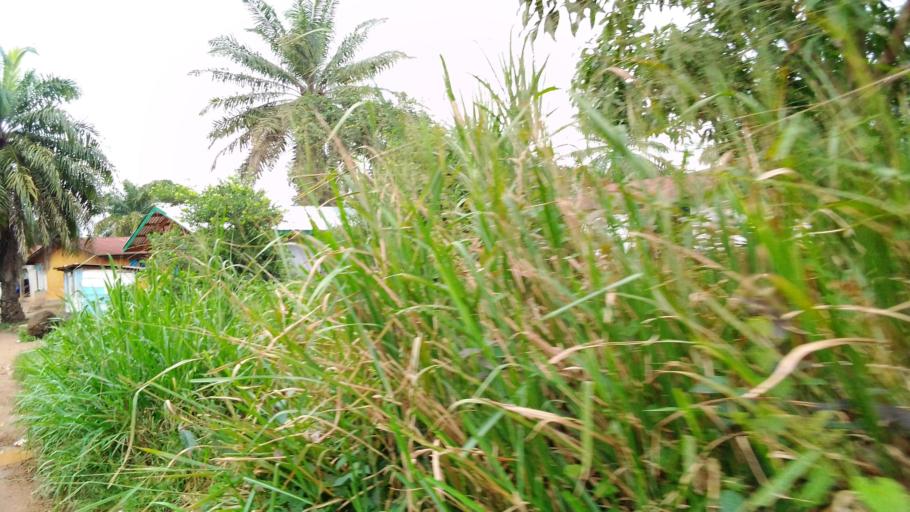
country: SL
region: Eastern Province
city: Kenema
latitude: 7.8551
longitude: -11.1868
